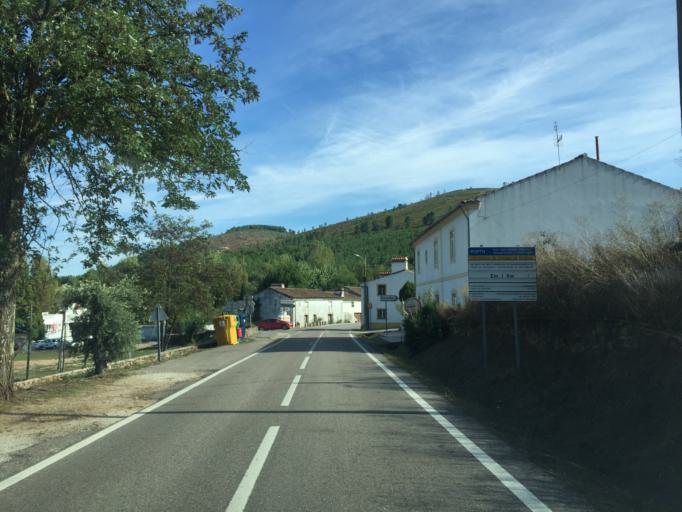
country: PT
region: Portalegre
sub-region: Marvao
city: Marvao
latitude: 39.3839
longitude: -7.3841
